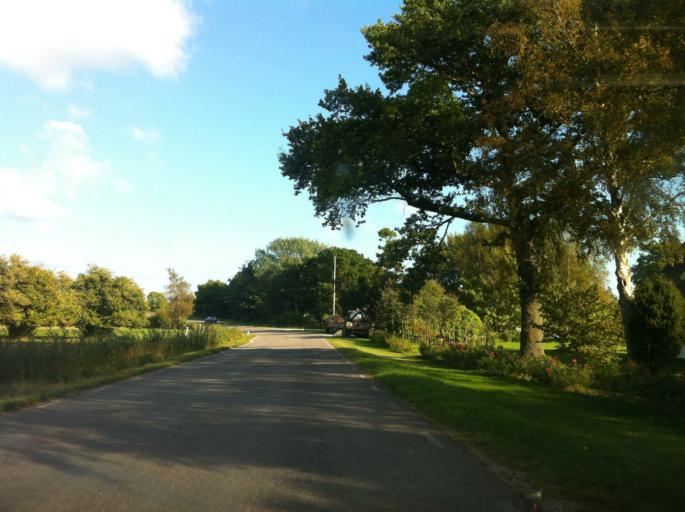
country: SE
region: Gotland
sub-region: Gotland
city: Slite
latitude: 57.4187
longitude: 18.8765
